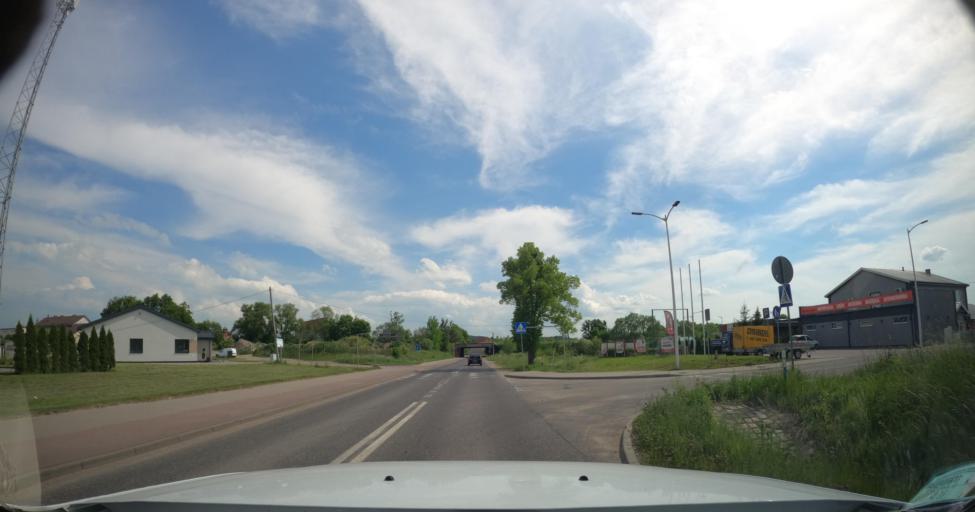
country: PL
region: Warmian-Masurian Voivodeship
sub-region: Powiat lidzbarski
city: Lidzbark Warminski
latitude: 54.1328
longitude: 20.5654
